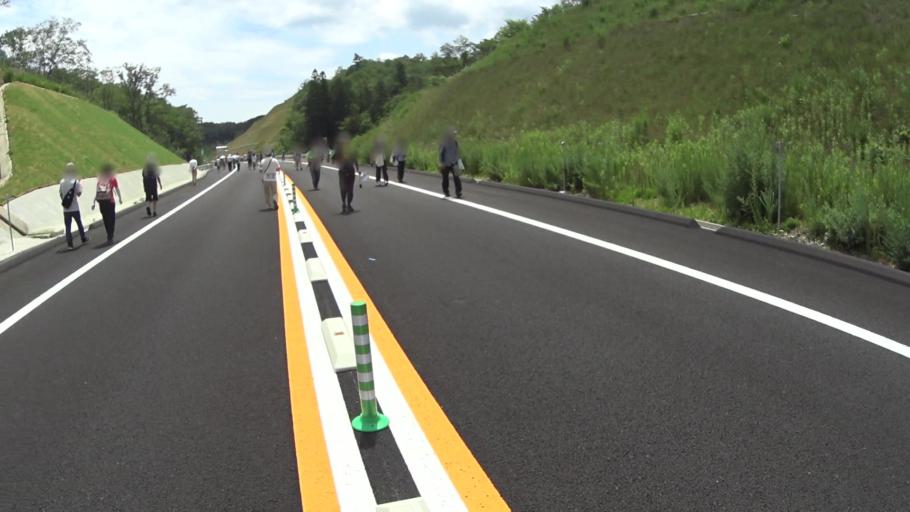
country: JP
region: Kyoto
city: Ayabe
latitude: 35.1693
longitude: 135.3733
